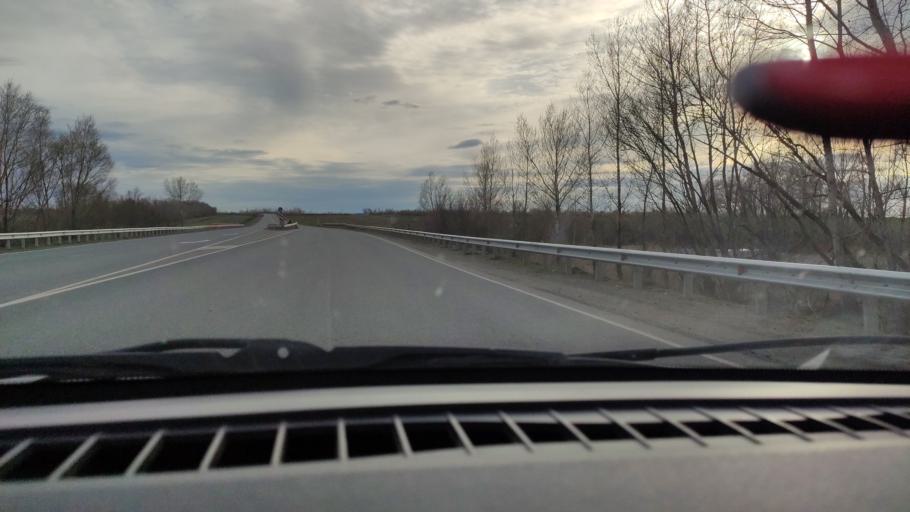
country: RU
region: Orenburg
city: Tatarskaya Kargala
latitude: 52.0224
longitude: 55.2186
